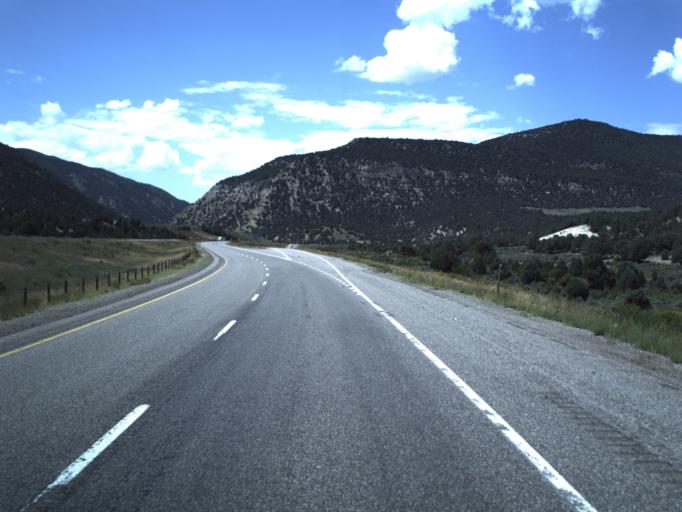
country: US
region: Utah
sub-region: Sevier County
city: Salina
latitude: 38.8772
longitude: -111.5576
